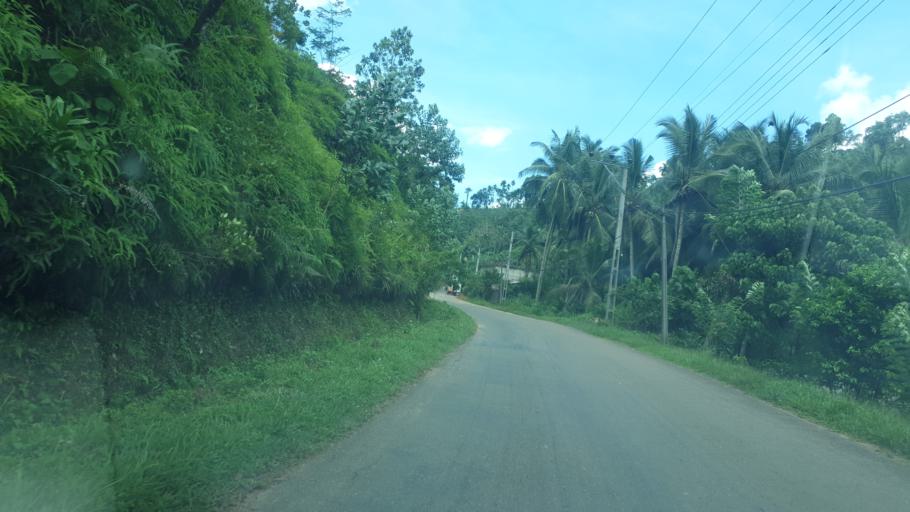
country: LK
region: Sabaragamuwa
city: Ratnapura
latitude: 6.4882
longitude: 80.4009
